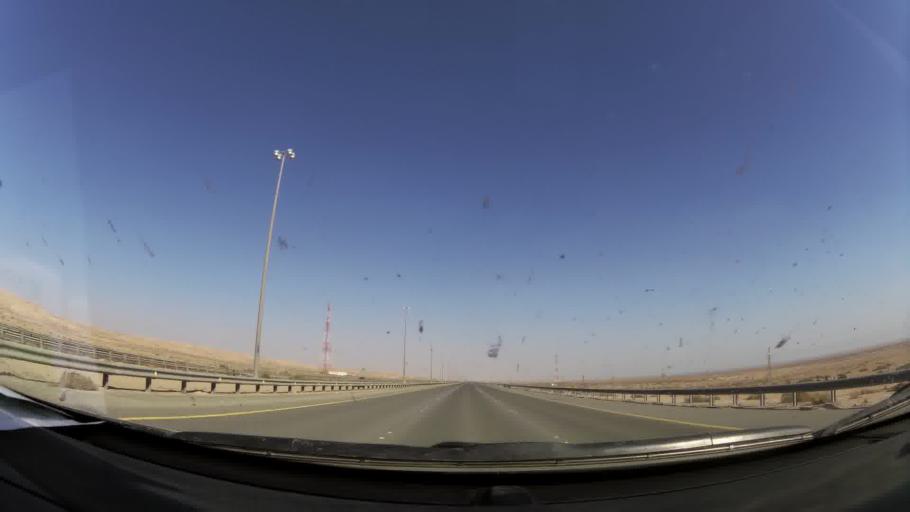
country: KW
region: Al Asimah
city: Kuwait City
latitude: 29.5312
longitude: 47.8282
